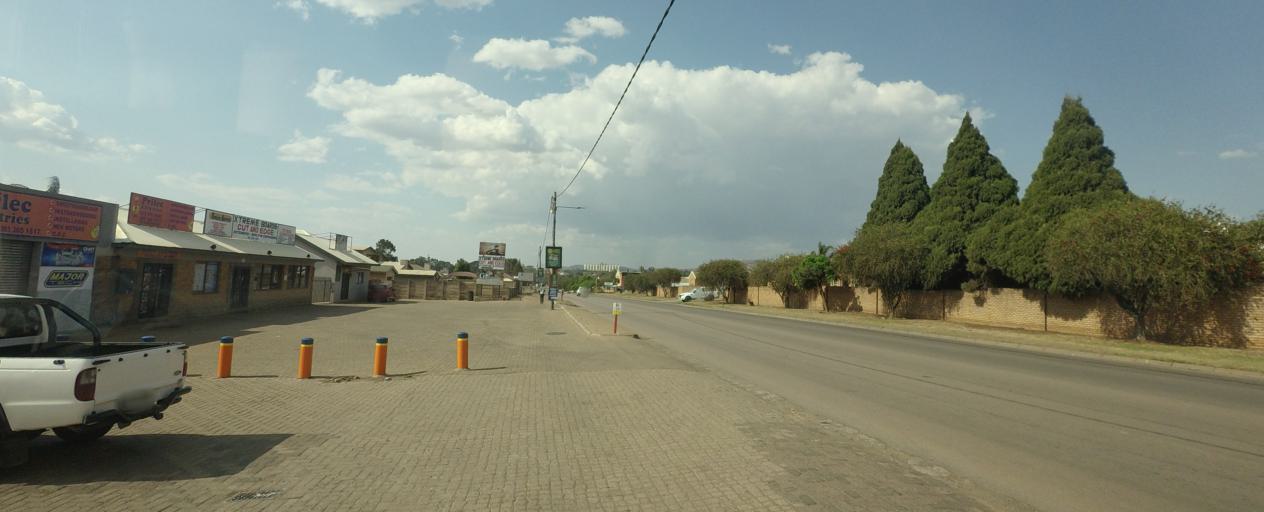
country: ZA
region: Mpumalanga
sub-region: Ehlanzeni District
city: Lydenburg
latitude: -25.1064
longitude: 30.4505
